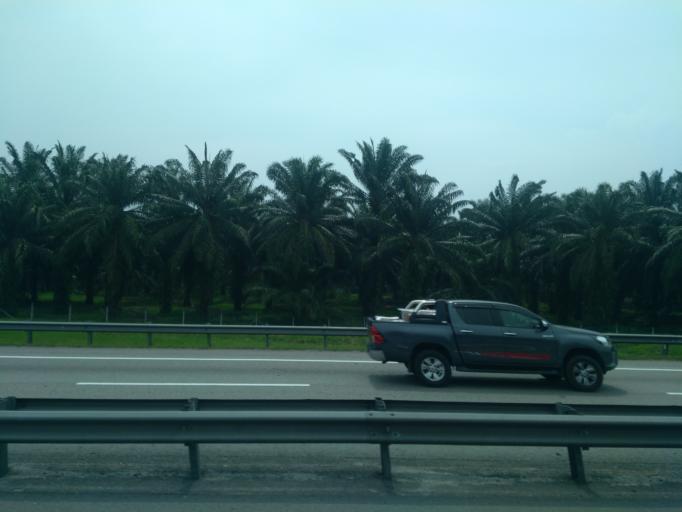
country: MY
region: Perak
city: Simpang Empat
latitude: 4.9069
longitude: 100.6686
